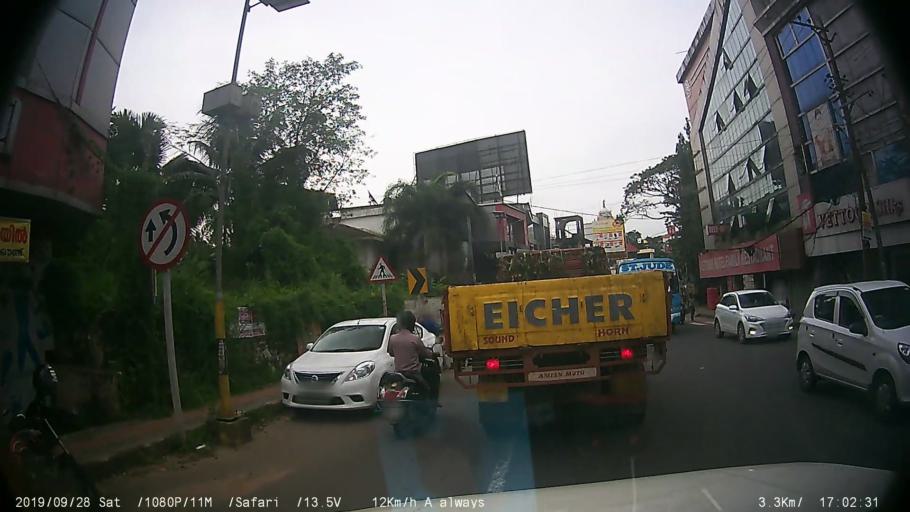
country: IN
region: Kerala
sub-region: Kottayam
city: Kottayam
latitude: 9.6700
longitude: 76.5544
